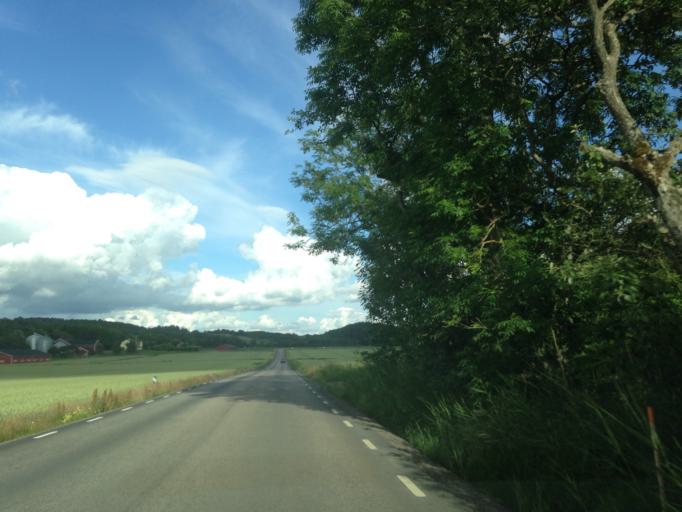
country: SE
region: Halland
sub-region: Kungsbacka Kommun
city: Fjaeras kyrkby
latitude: 57.4836
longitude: 12.1440
